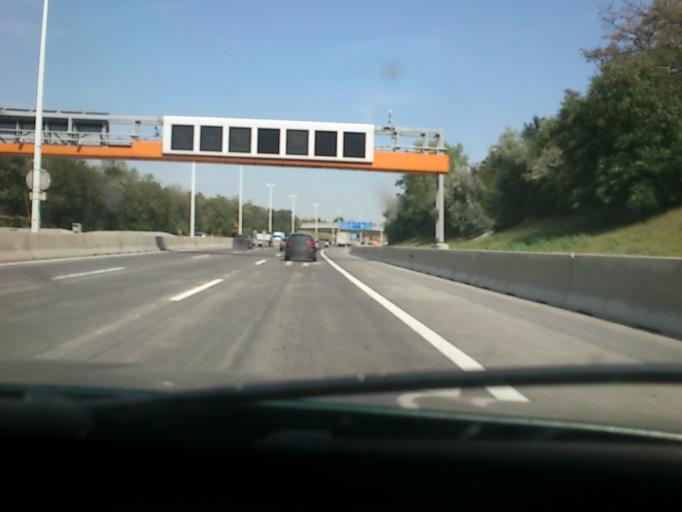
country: AT
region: Lower Austria
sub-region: Politischer Bezirk Wien-Umgebung
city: Leopoldsdorf
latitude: 48.1540
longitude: 16.3751
